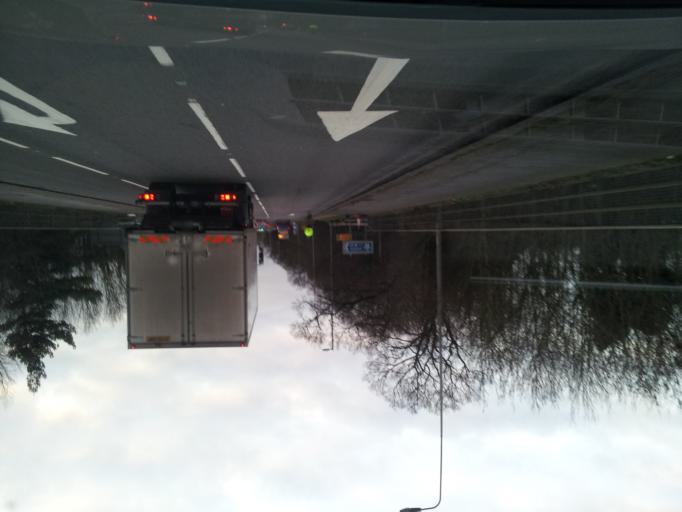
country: GB
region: England
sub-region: Cambridgeshire
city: Girton
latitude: 52.2144
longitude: 0.0781
